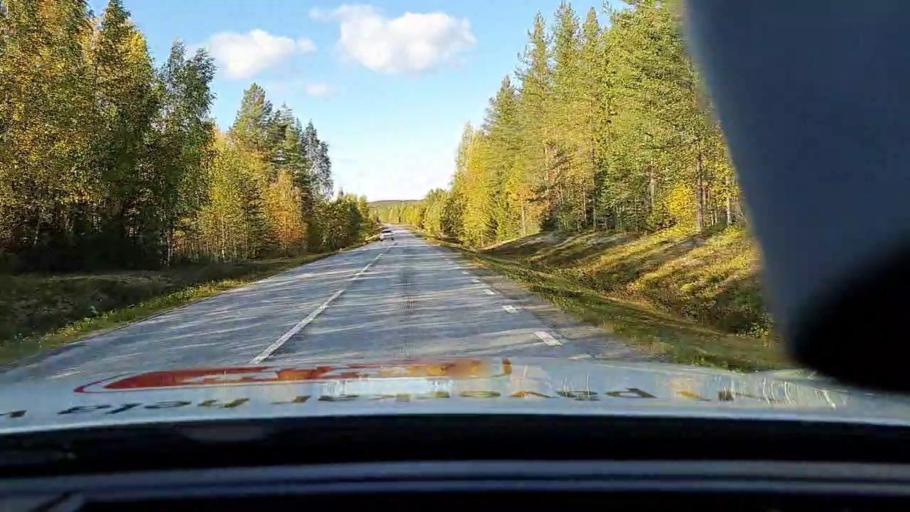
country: SE
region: Norrbotten
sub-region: Pitea Kommun
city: Norrfjarden
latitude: 65.4569
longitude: 21.4550
